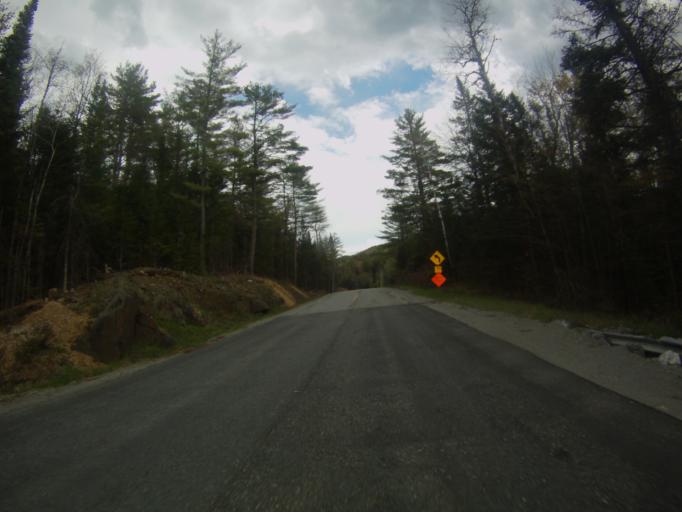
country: US
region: New York
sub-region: Essex County
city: Mineville
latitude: 44.0784
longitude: -73.6078
